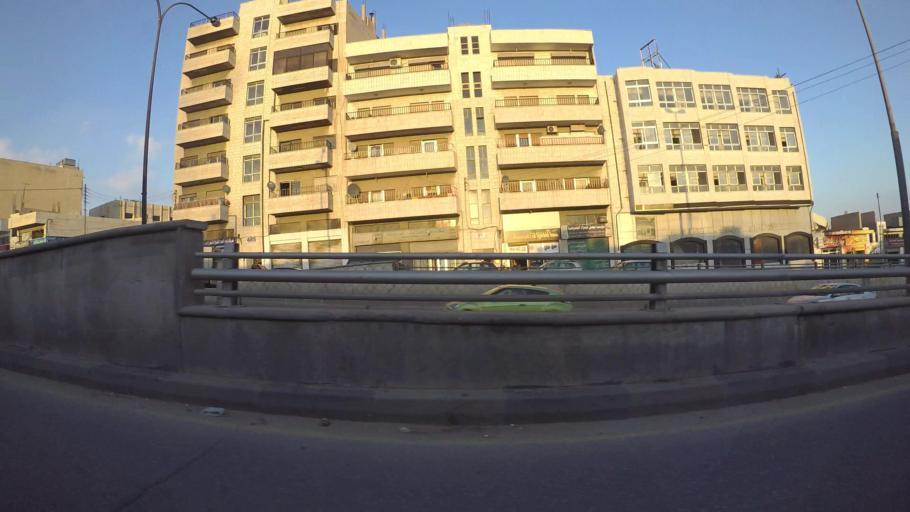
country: JO
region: Amman
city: Al Quwaysimah
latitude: 31.9029
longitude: 35.9372
